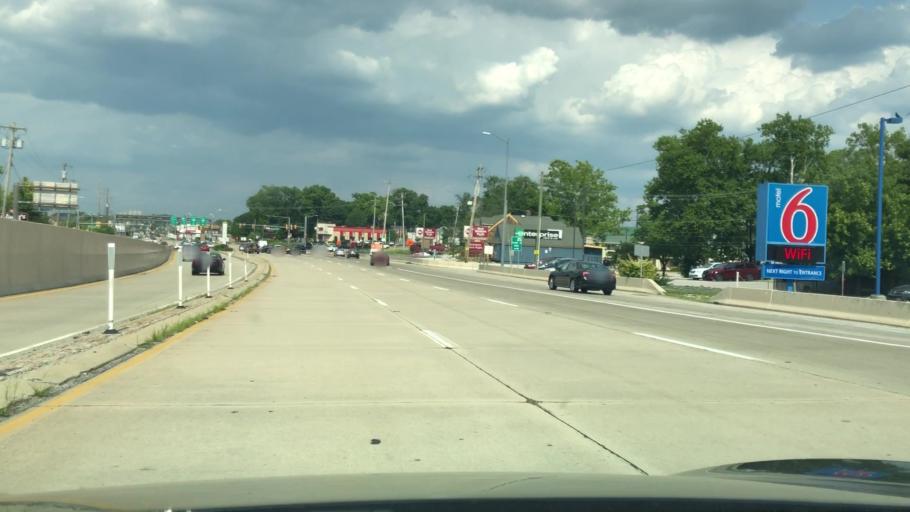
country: US
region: Pennsylvania
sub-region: Montgomery County
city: King of Prussia
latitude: 40.0842
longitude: -75.3912
